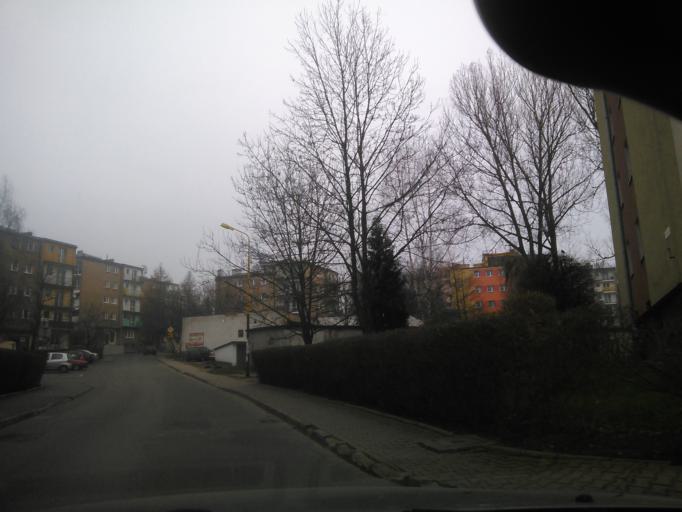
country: PL
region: Lower Silesian Voivodeship
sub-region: Jelenia Gora
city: Jelenia Gora
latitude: 50.8978
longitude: 15.7431
